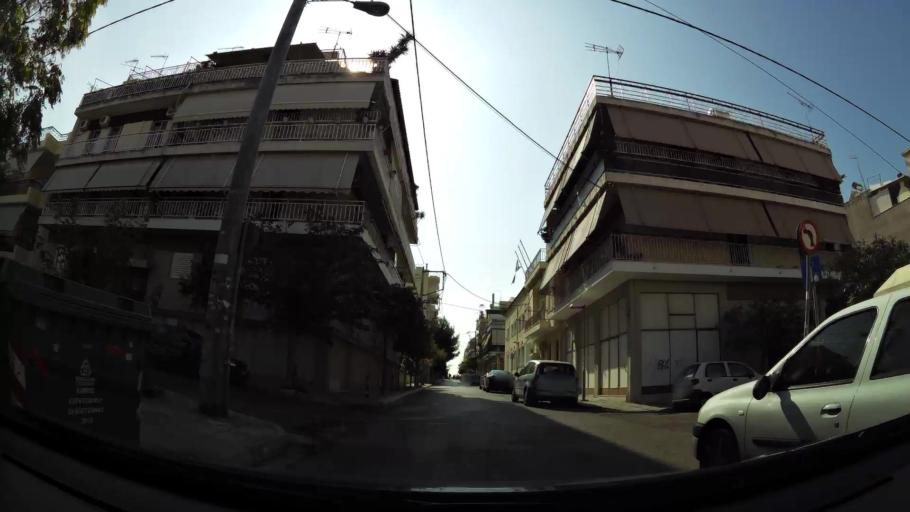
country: GR
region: Attica
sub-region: Nomos Piraios
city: Drapetsona
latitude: 37.9507
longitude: 23.6241
